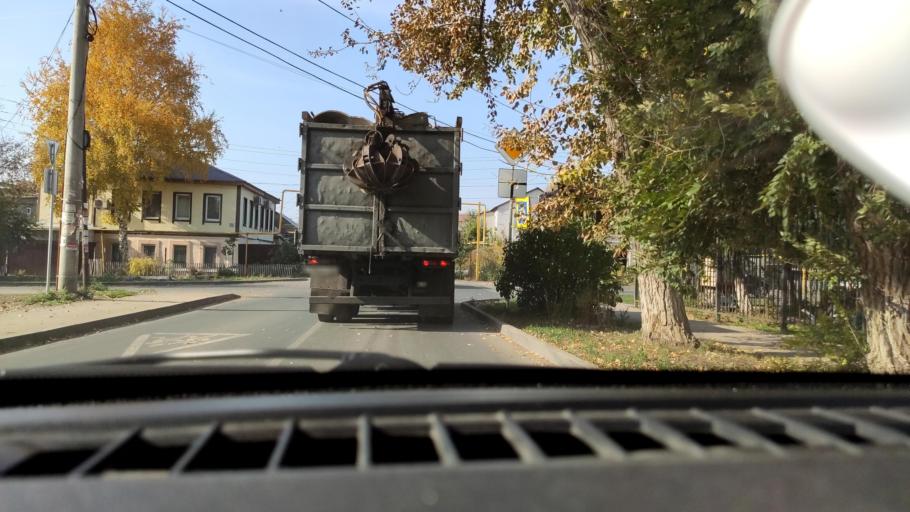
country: RU
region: Samara
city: Samara
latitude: 53.1805
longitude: 50.1346
